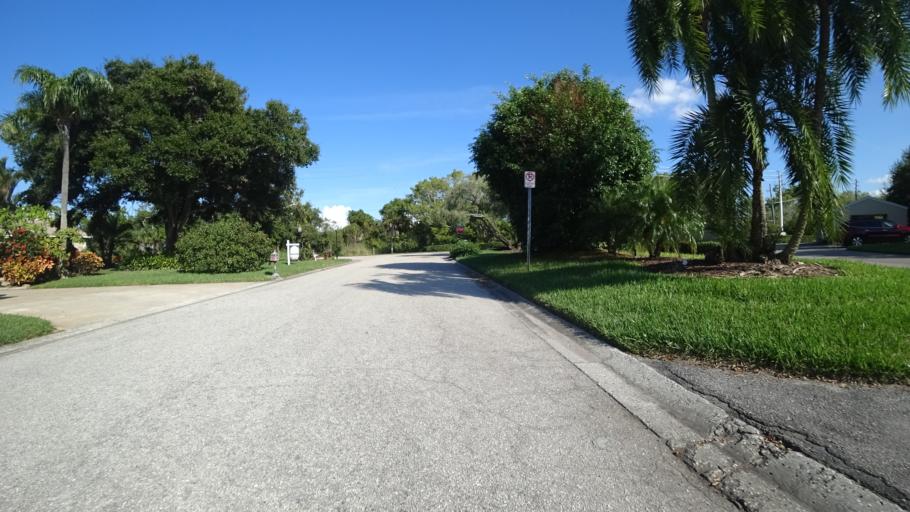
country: US
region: Florida
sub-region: Manatee County
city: Longboat Key
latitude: 27.4509
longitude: -82.6491
